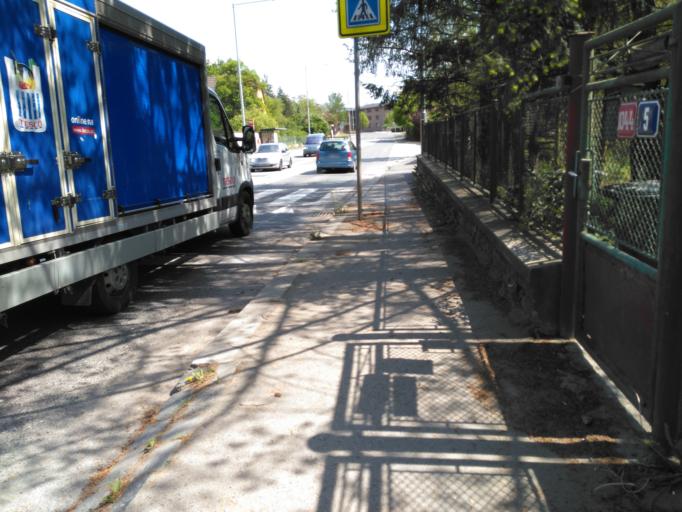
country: CZ
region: Central Bohemia
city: Cernosice
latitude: 49.9902
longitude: 14.3498
